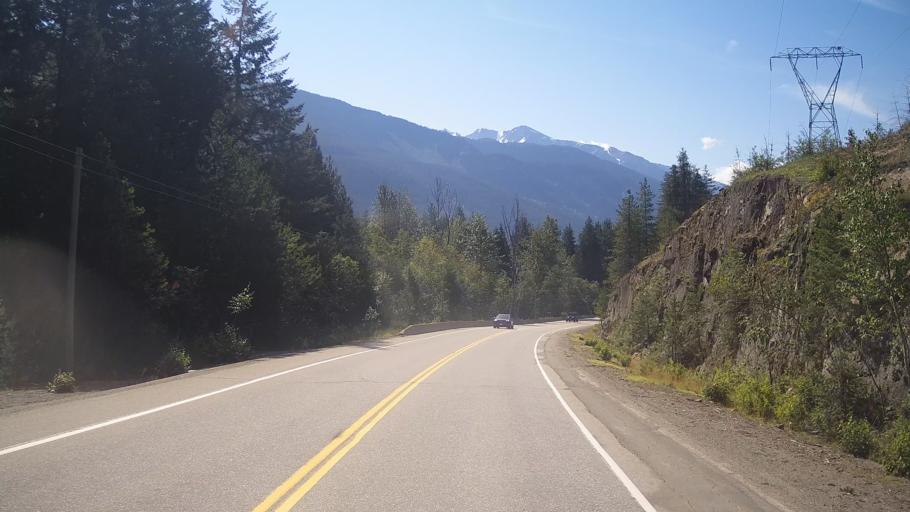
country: CA
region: British Columbia
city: Pemberton
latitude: 50.2639
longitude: -122.8659
